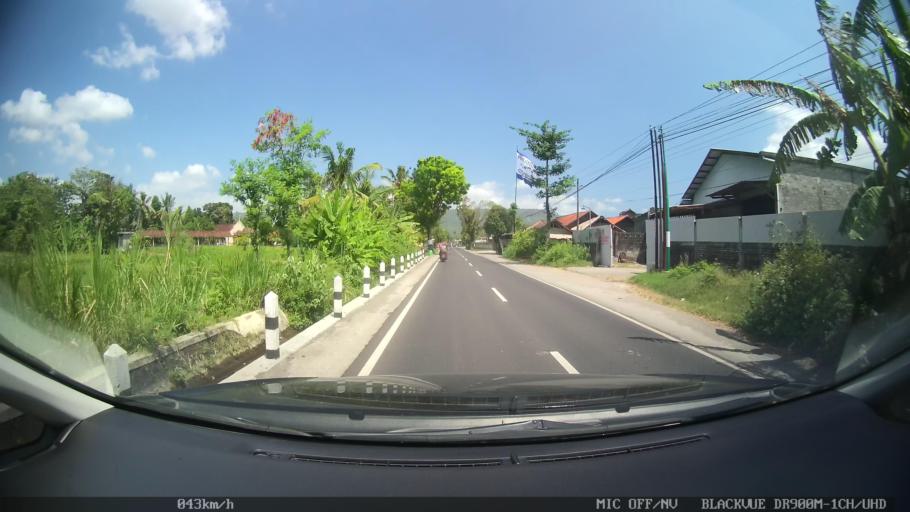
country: ID
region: Daerah Istimewa Yogyakarta
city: Pundong
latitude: -7.9335
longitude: 110.3738
